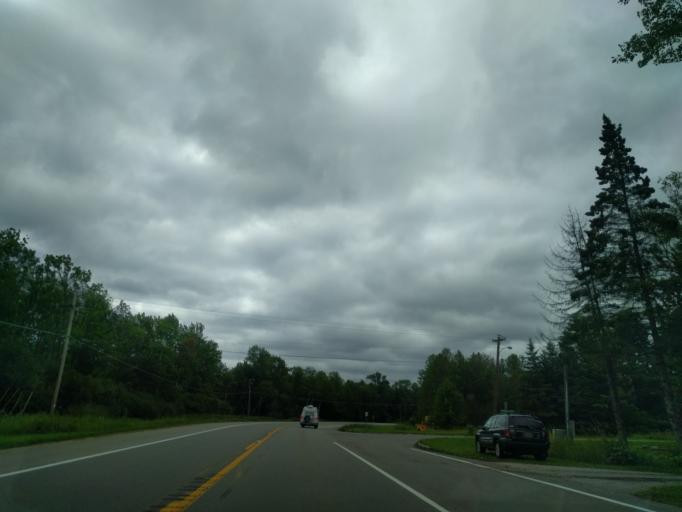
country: US
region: Michigan
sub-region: Menominee County
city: Menominee
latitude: 45.1588
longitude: -87.5911
